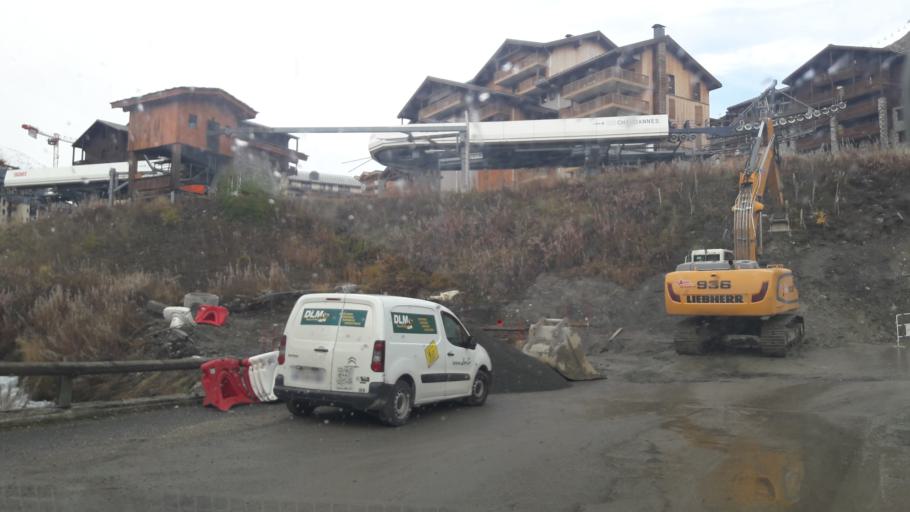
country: FR
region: Rhone-Alpes
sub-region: Departement de la Savoie
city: Tignes
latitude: 45.4725
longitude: 6.9113
